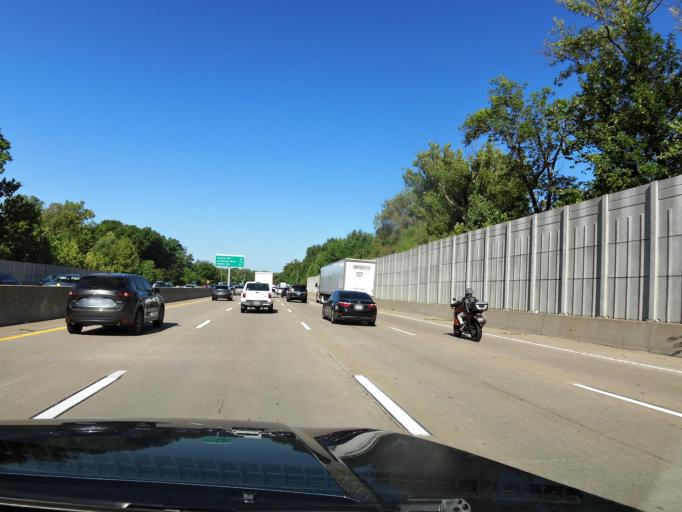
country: US
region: Missouri
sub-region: Saint Louis County
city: Ladue
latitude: 38.6316
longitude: -90.3766
